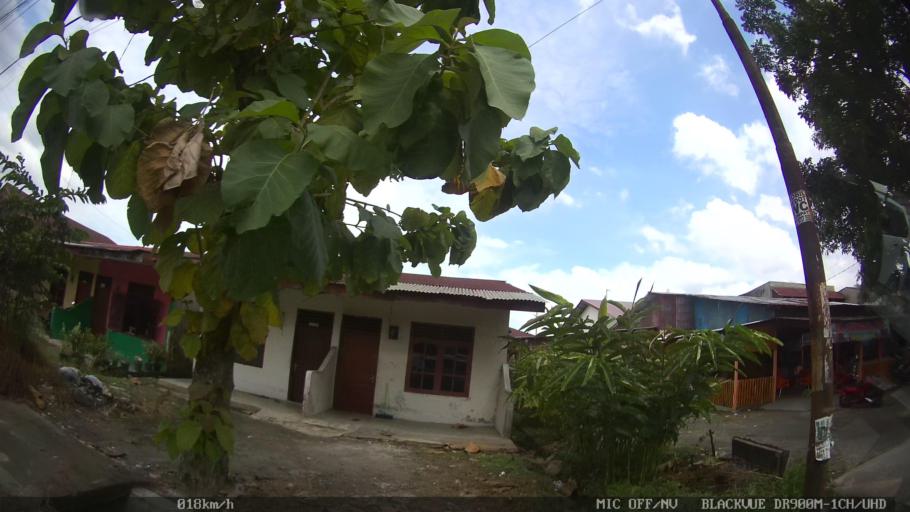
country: ID
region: North Sumatra
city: Sunggal
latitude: 3.6116
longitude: 98.6238
